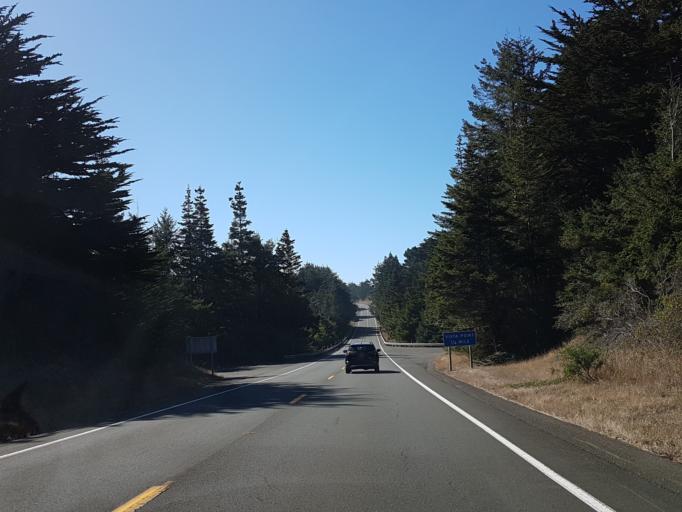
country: US
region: California
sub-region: Mendocino County
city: Boonville
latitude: 39.0362
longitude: -123.6867
